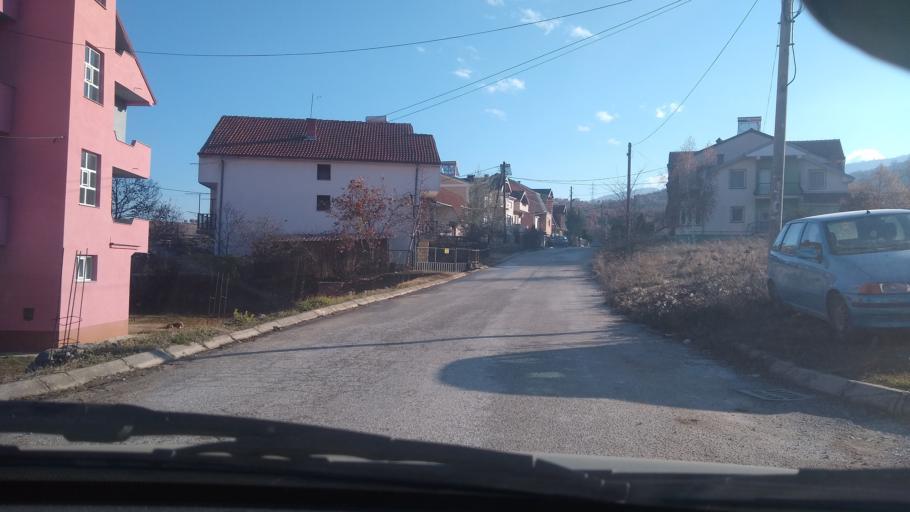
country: MK
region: Bitola
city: Bitola
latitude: 41.0186
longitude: 21.3140
